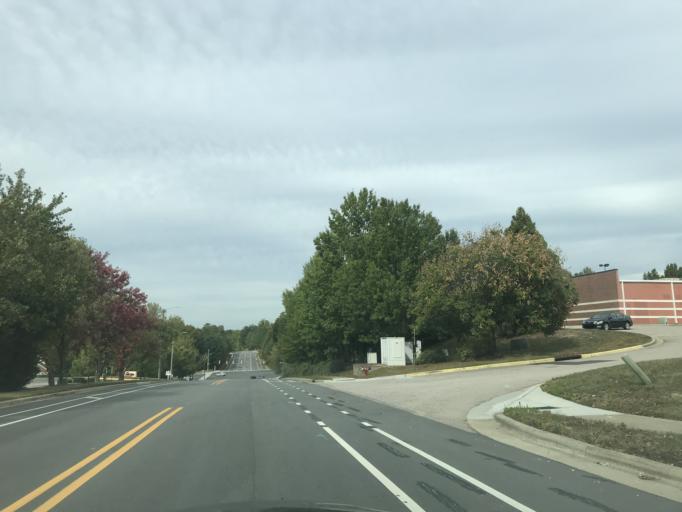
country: US
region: North Carolina
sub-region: Wake County
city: Wake Forest
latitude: 35.9436
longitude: -78.5448
